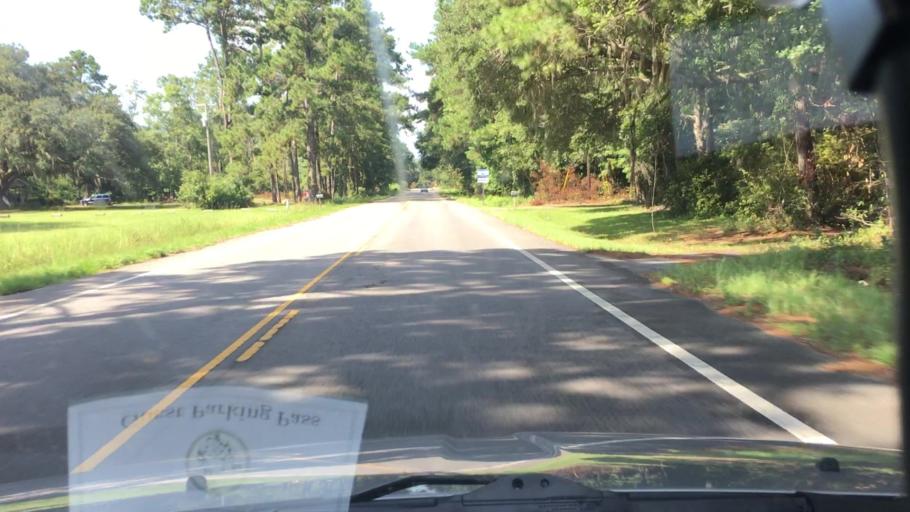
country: US
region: South Carolina
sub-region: Beaufort County
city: Beaufort
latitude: 32.4040
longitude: -80.5345
